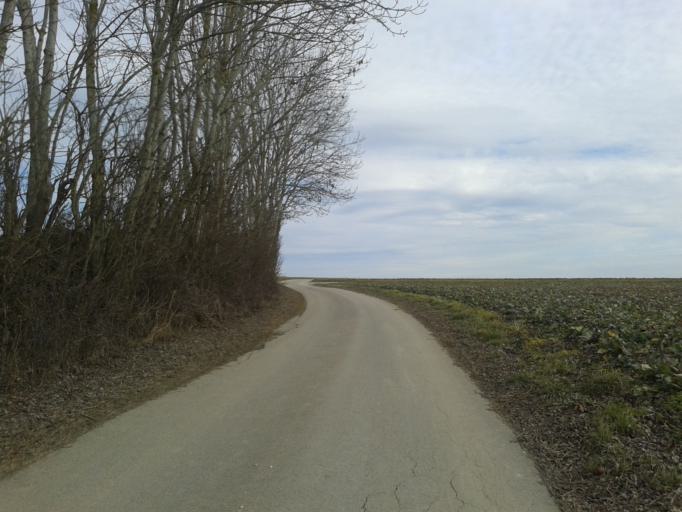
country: DE
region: Baden-Wuerttemberg
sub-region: Tuebingen Region
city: Altheim
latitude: 48.3328
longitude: 9.7770
